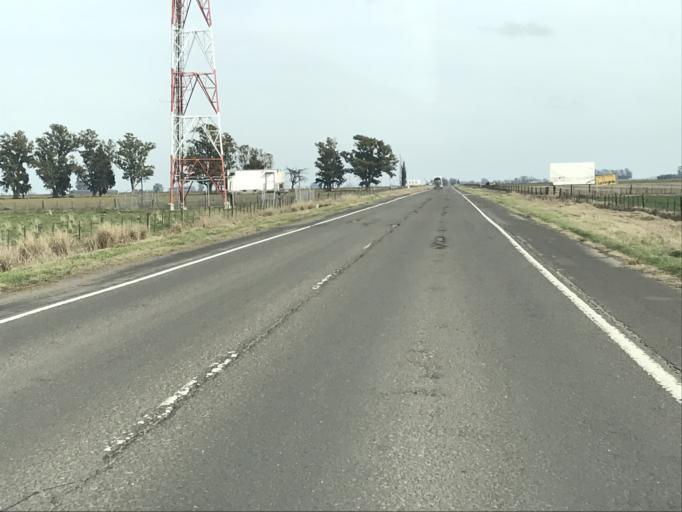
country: AR
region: Santa Fe
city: Armstrong
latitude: -32.7658
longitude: -61.6534
